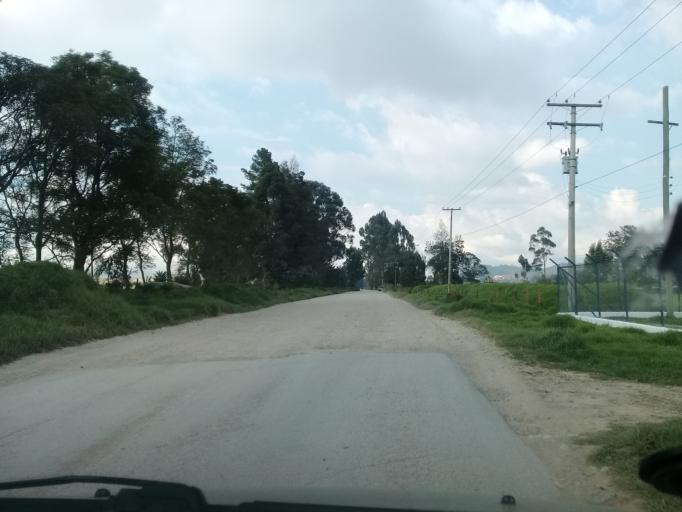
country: CO
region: Cundinamarca
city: Funza
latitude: 4.7650
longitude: -74.2208
